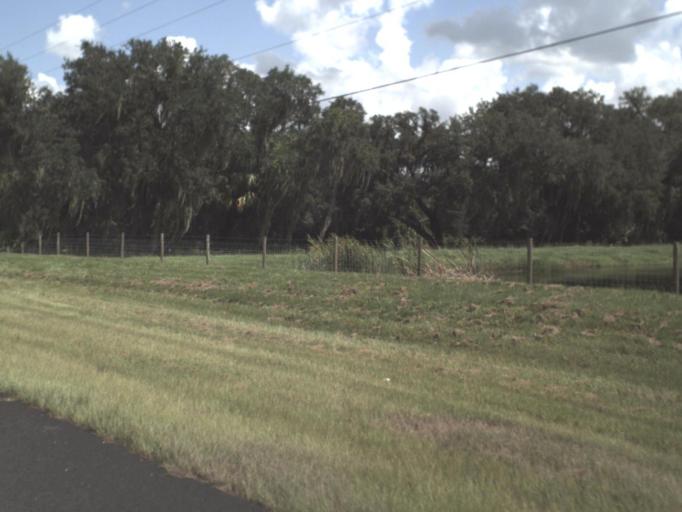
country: US
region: Florida
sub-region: Hardee County
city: Zolfo Springs
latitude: 27.4750
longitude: -81.7977
